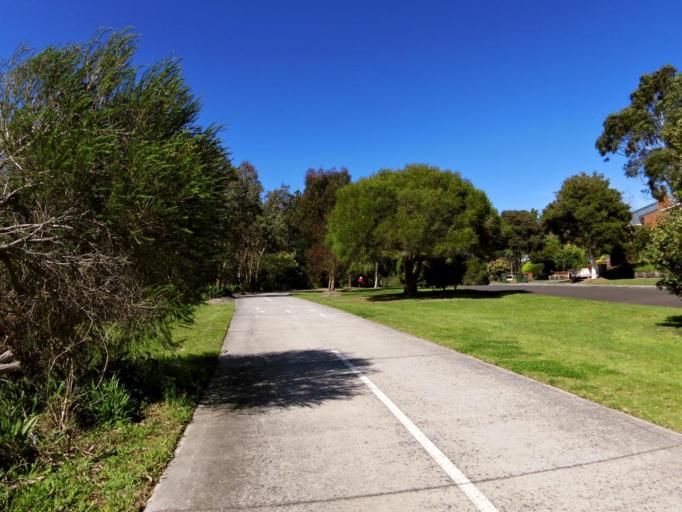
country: AU
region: Victoria
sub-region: Monash
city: Mulgrave
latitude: -37.9265
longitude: 145.2049
